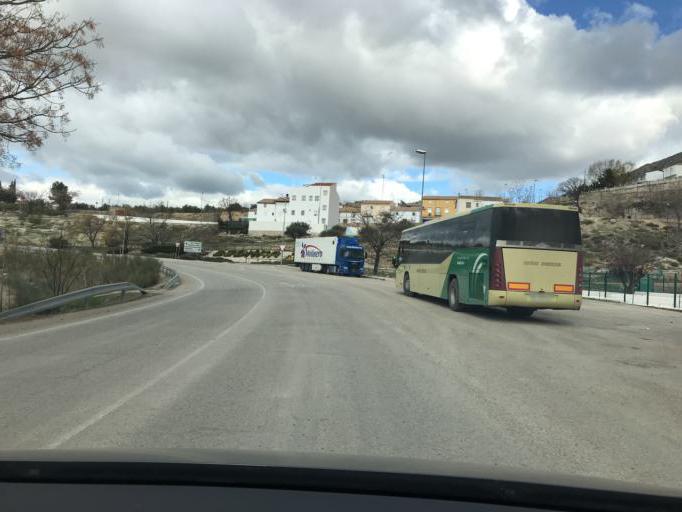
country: ES
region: Andalusia
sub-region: Provincia de Jaen
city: Jodar
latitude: 37.8255
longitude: -3.4139
